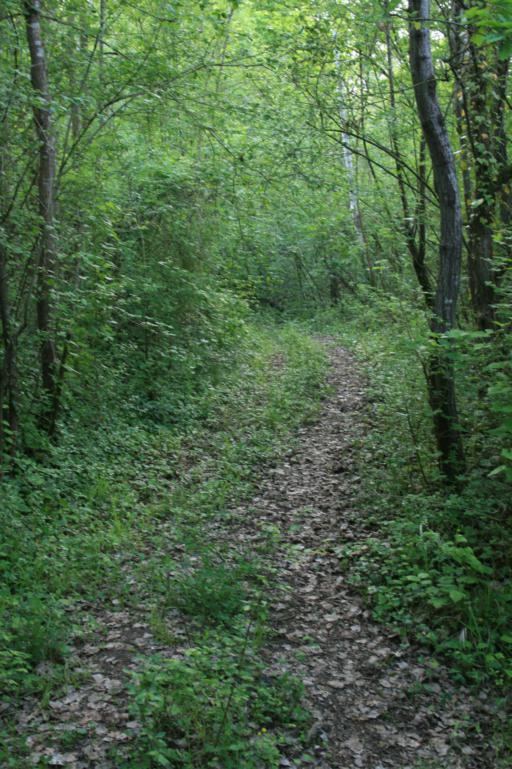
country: FR
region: Ile-de-France
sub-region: Departement des Yvelines
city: Vaux-sur-Seine
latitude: 48.9983
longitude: 1.9857
